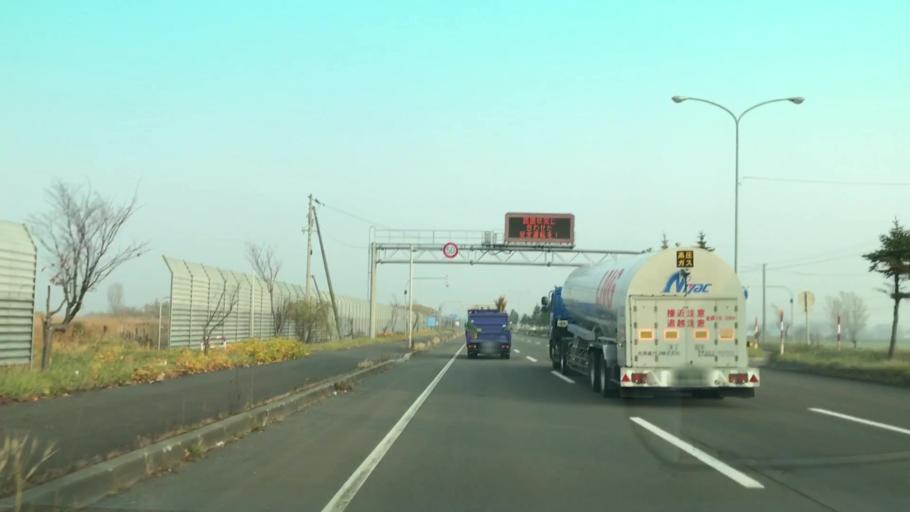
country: JP
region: Hokkaido
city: Ishikari
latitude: 43.1716
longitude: 141.3484
